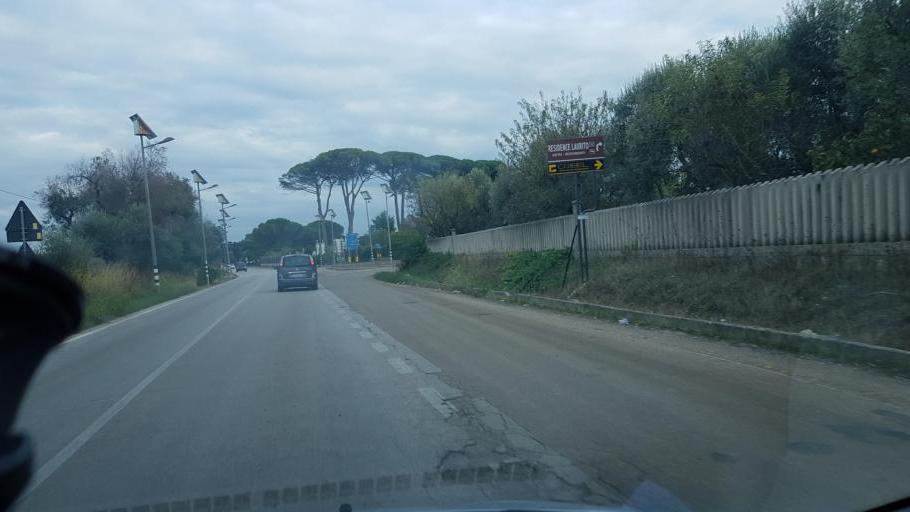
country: IT
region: Apulia
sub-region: Provincia di Brindisi
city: Francavilla Fontana
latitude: 40.5165
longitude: 17.6115
